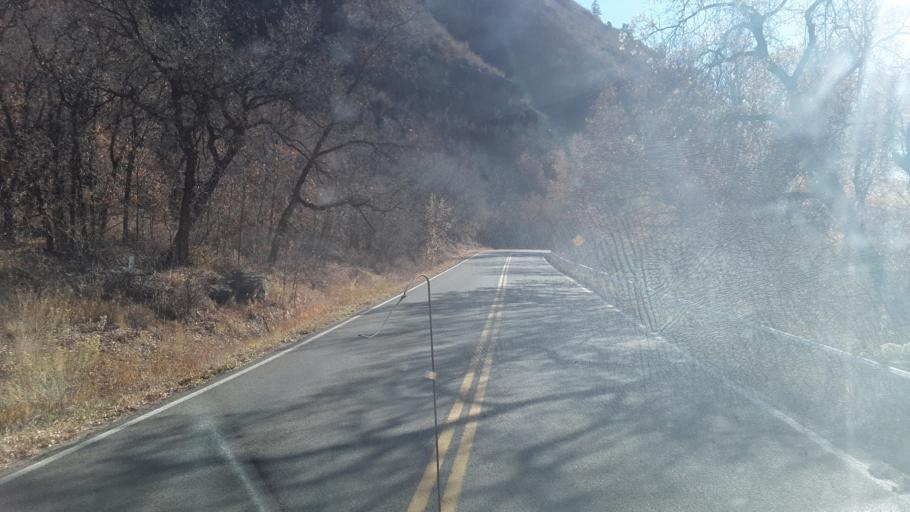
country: US
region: Colorado
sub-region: La Plata County
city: Durango
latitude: 37.3927
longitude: -107.8244
